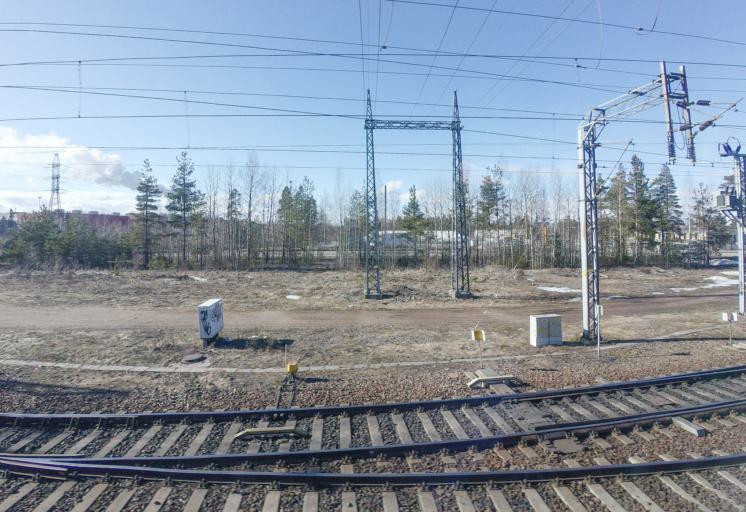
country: FI
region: South Karelia
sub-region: Lappeenranta
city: Lappeenranta
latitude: 61.0649
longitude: 28.2578
